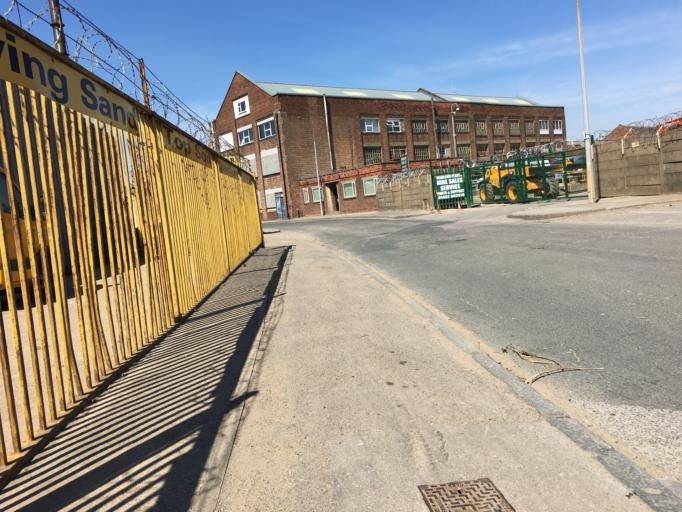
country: GB
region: England
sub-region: City of Kingston upon Hull
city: Hull
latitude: 53.7555
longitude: -0.3309
